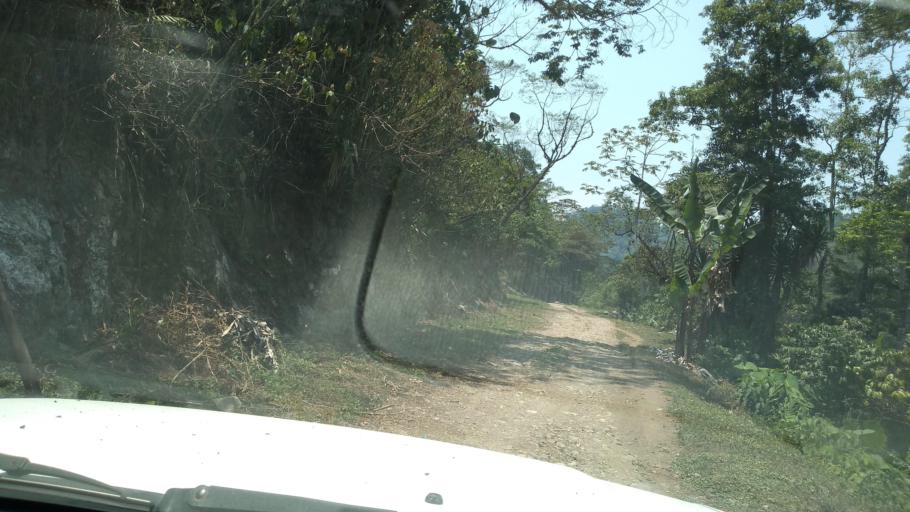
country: MX
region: Veracruz
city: Motzorongo
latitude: 18.6188
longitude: -96.7583
